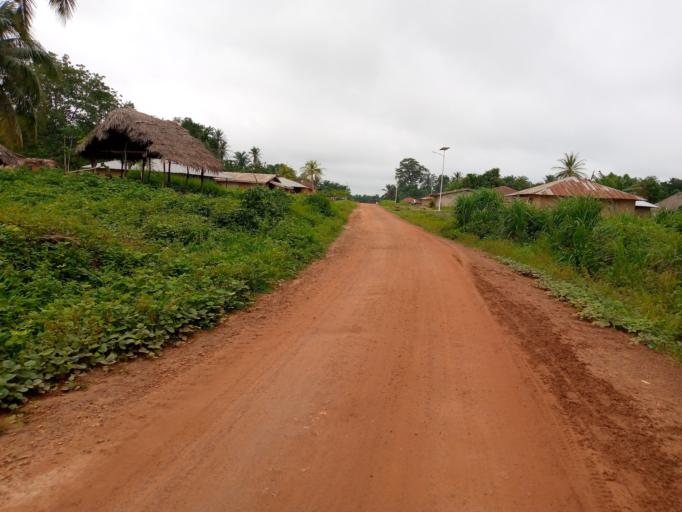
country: SL
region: Southern Province
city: Sumbuya
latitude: 7.5969
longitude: -12.0844
